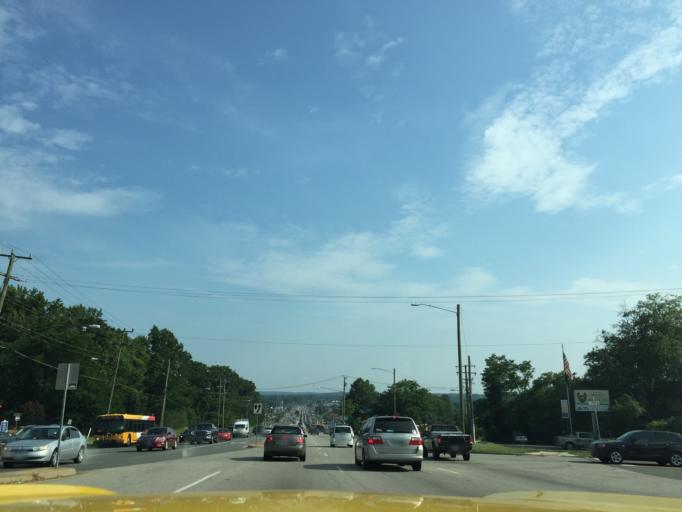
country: US
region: Virginia
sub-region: Fairfax County
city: Groveton
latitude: 38.7631
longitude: -77.0842
